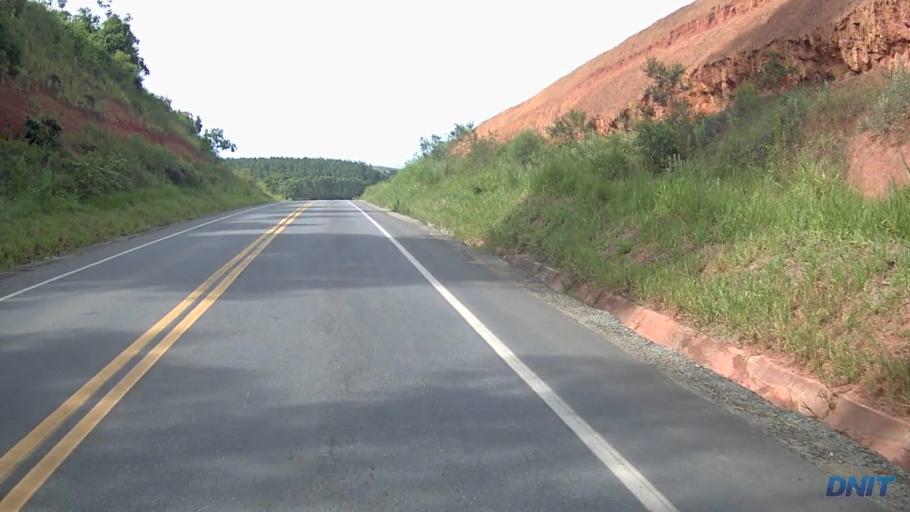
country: BR
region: Minas Gerais
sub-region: Belo Oriente
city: Belo Oriente
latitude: -19.2492
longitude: -42.3388
